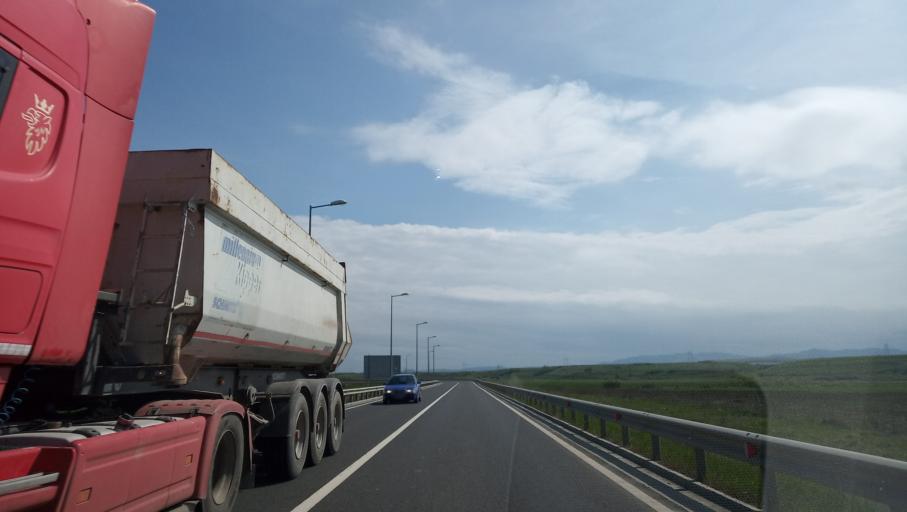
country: RO
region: Hunedoara
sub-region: Comuna Romos
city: Romos
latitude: 45.8876
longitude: 23.2598
